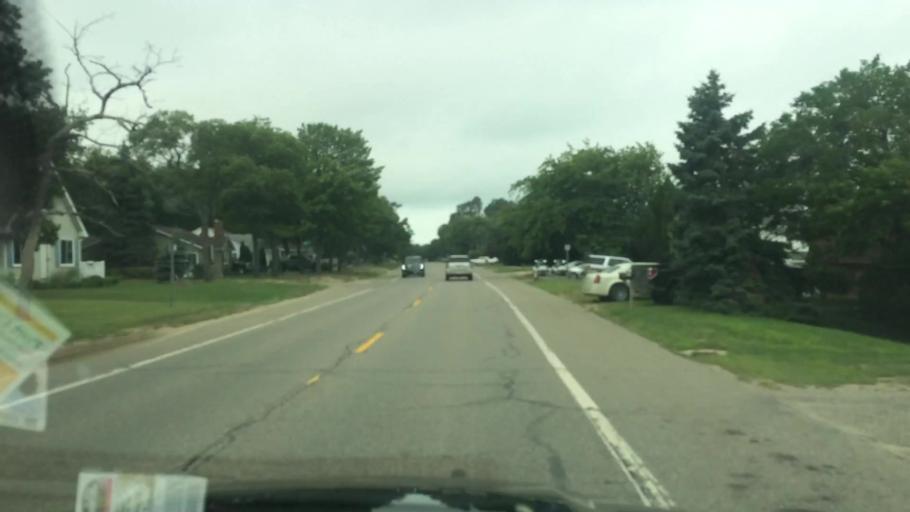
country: US
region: Michigan
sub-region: Huron County
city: Pigeon
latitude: 43.9775
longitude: -83.2398
